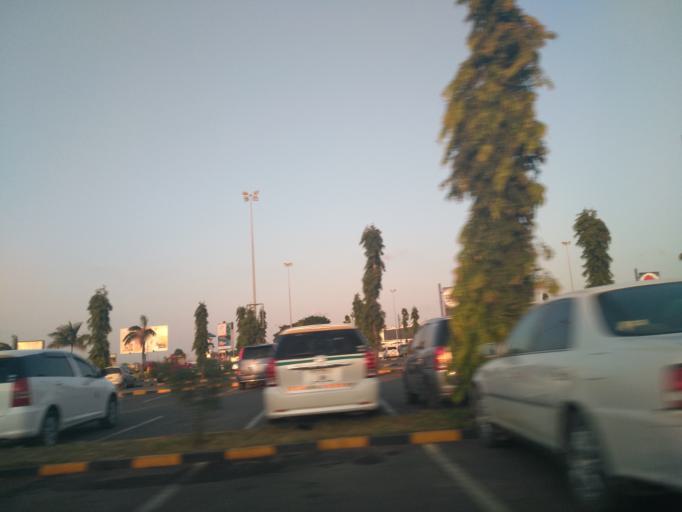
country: TZ
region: Dar es Salaam
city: Dar es Salaam
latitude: -6.8658
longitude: 39.2066
